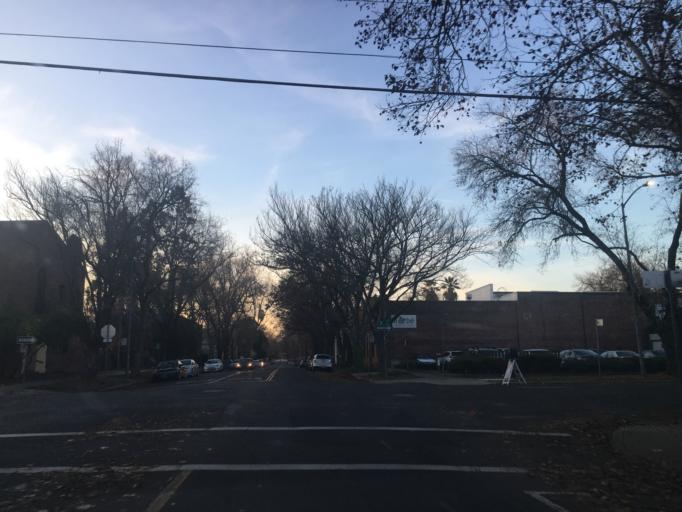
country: US
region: California
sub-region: Sacramento County
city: Sacramento
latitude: 38.5711
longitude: -121.5001
